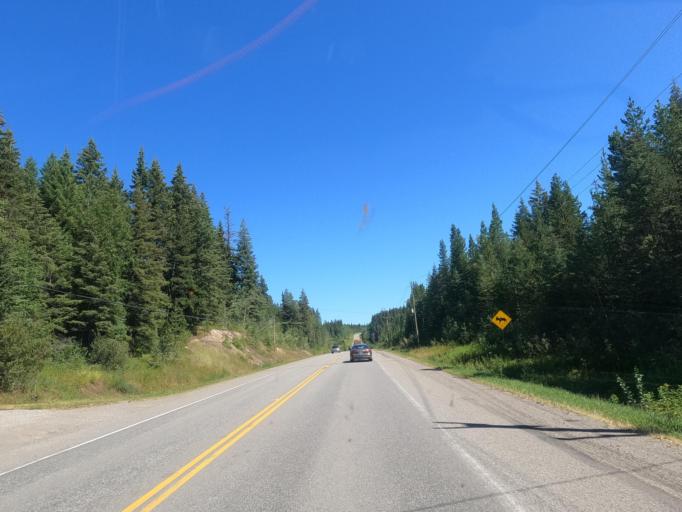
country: CA
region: British Columbia
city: Quesnel
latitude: 53.0536
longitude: -122.4523
